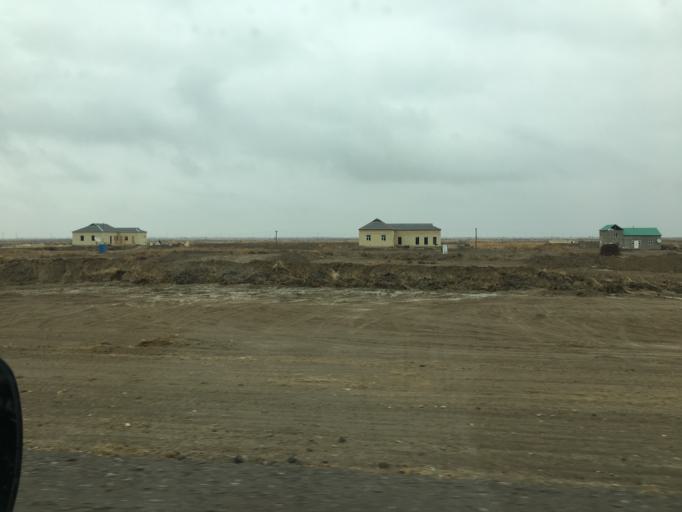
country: TM
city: Murgab
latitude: 37.4741
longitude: 62.0203
